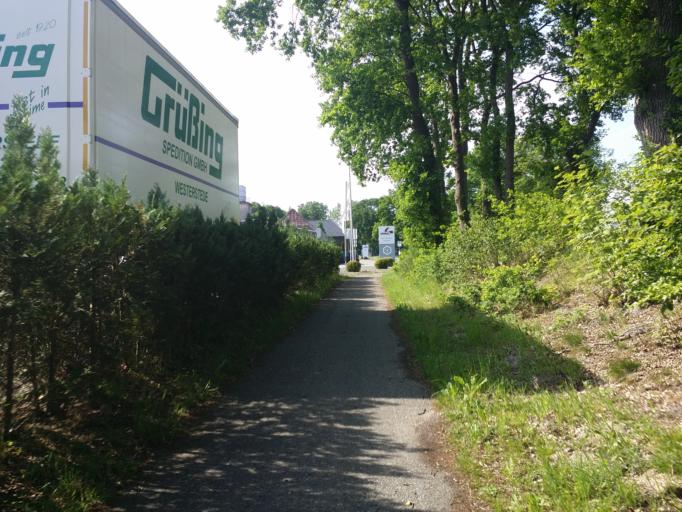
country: DE
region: Lower Saxony
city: Wiefelstede
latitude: 53.2922
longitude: 8.0701
